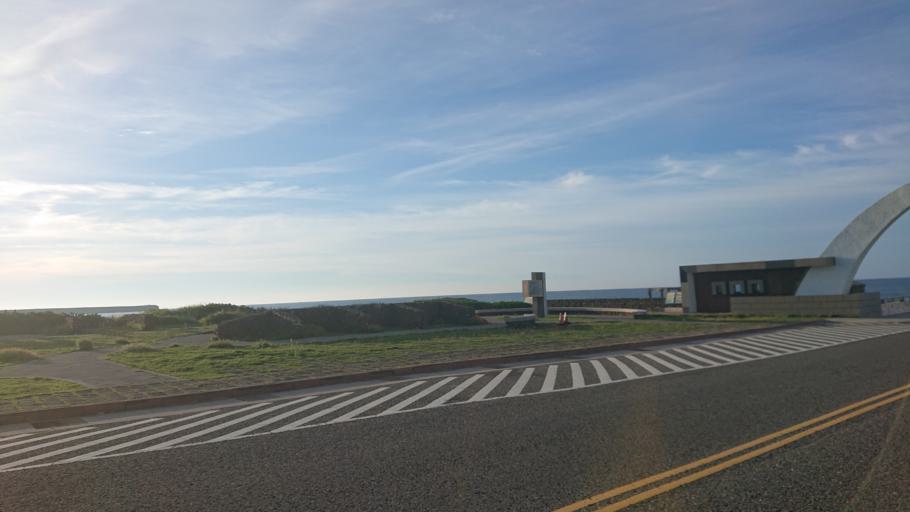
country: TW
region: Taiwan
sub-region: Penghu
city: Ma-kung
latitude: 23.6395
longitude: 119.5399
